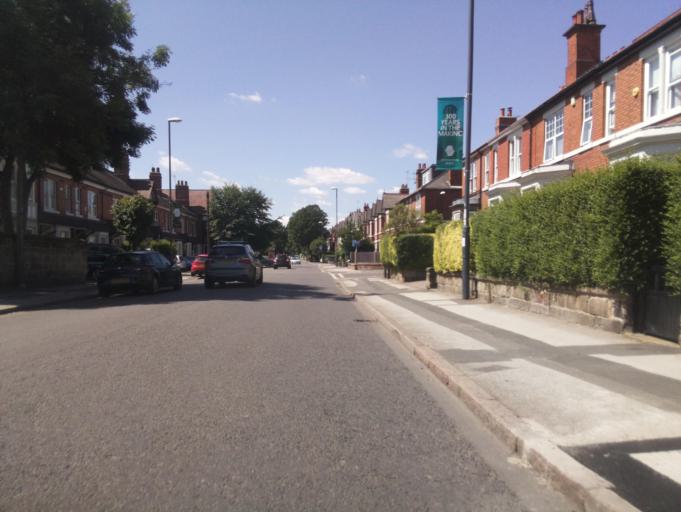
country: GB
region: England
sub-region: Derby
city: Derby
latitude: 52.9315
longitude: -1.4887
